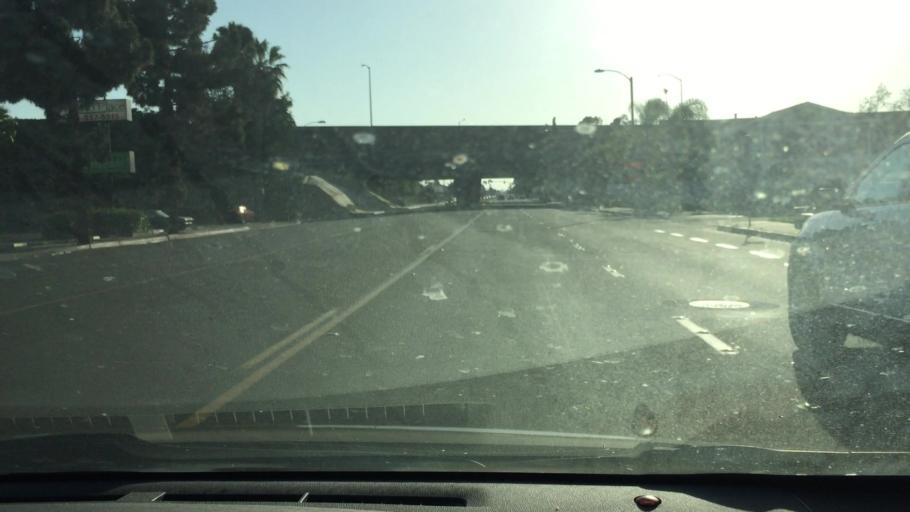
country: US
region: California
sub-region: Orange County
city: Costa Mesa
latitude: 33.6802
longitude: -117.8899
